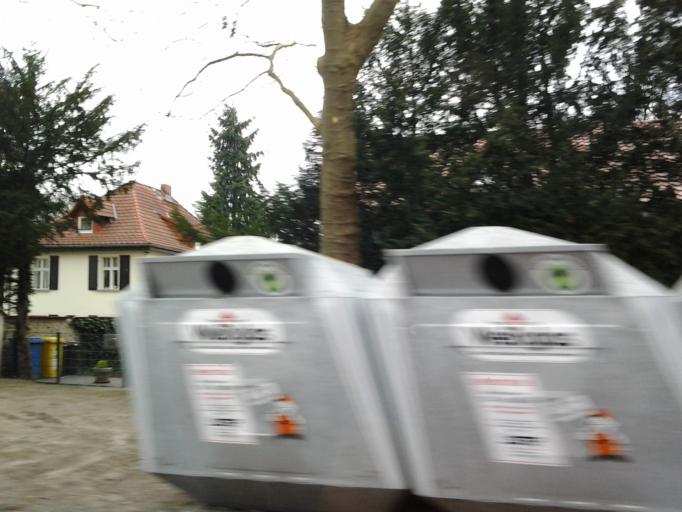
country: DE
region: Brandenburg
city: Potsdam
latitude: 52.4178
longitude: 13.0204
